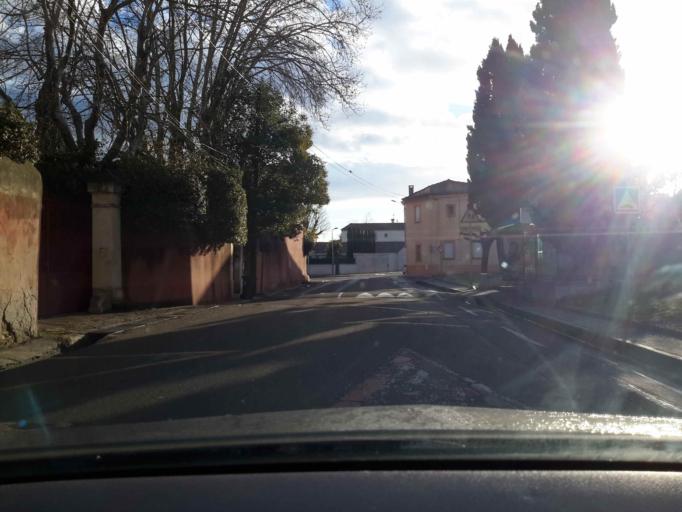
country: FR
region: Languedoc-Roussillon
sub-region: Departement du Gard
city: Generac
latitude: 43.7293
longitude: 4.3449
